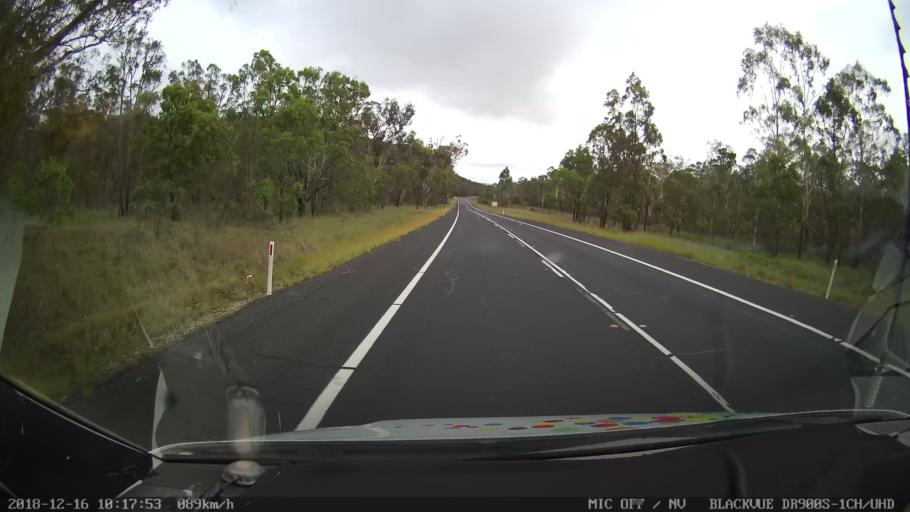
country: AU
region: New South Wales
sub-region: Tenterfield Municipality
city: Carrolls Creek
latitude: -29.2511
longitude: 151.9950
